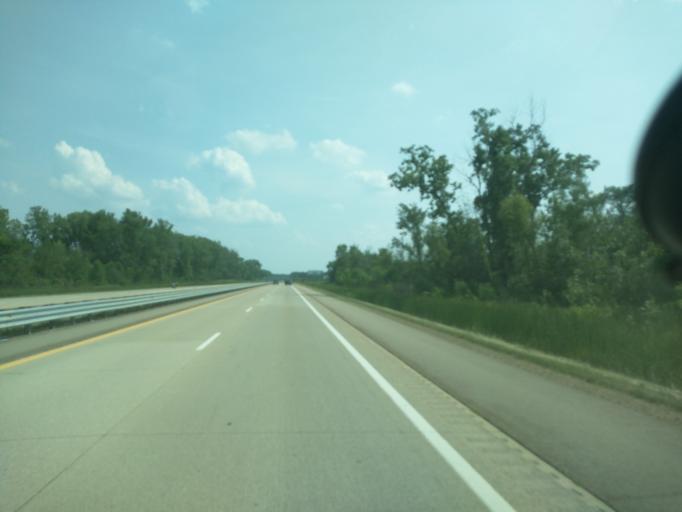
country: US
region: Michigan
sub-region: Jackson County
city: Jackson
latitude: 42.3358
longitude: -84.4290
